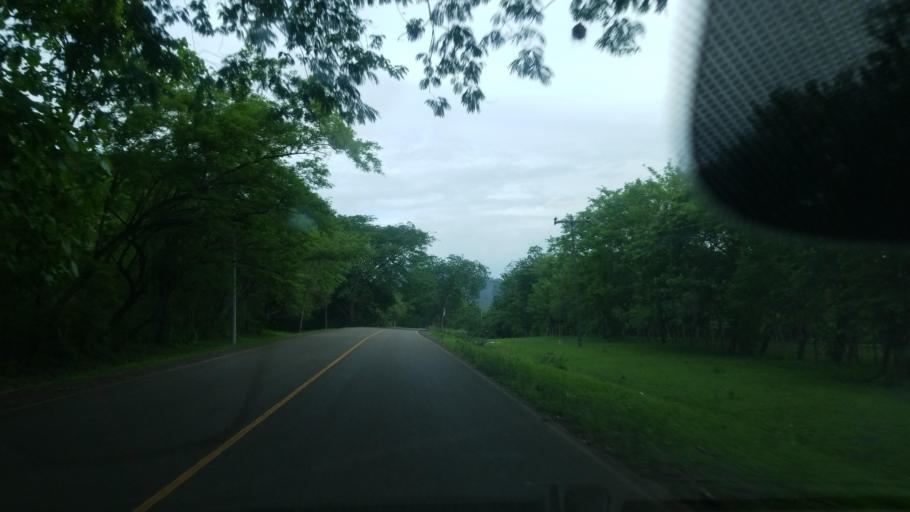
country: HN
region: Santa Barbara
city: San Vicente Centenario
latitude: 14.8745
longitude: -88.2482
